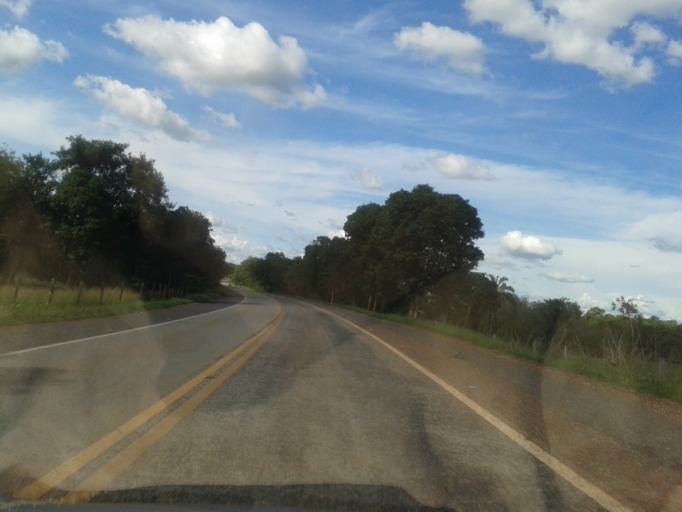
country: BR
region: Goias
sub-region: Mozarlandia
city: Mozarlandia
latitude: -14.9852
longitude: -50.5815
